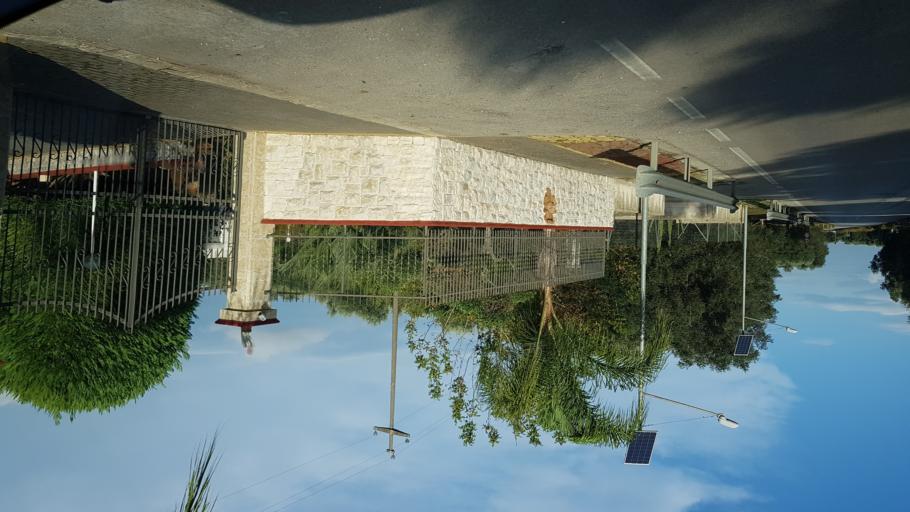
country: IT
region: Apulia
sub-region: Provincia di Brindisi
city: Oria
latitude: 40.5277
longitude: 17.6542
